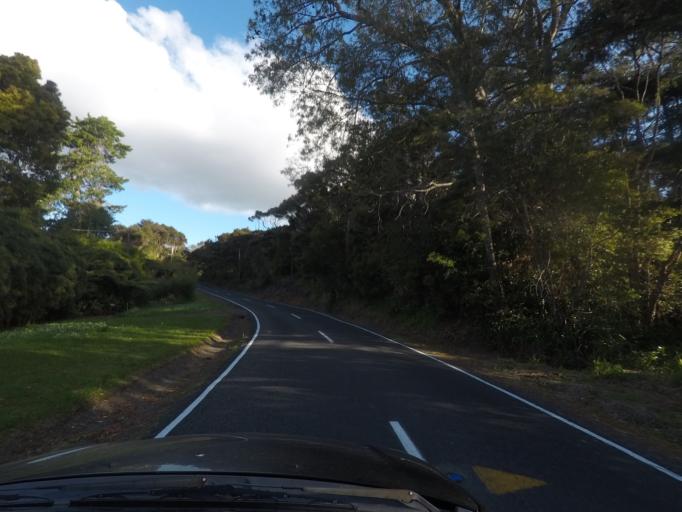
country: NZ
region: Auckland
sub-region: Auckland
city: Titirangi
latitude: -36.9255
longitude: 174.6189
